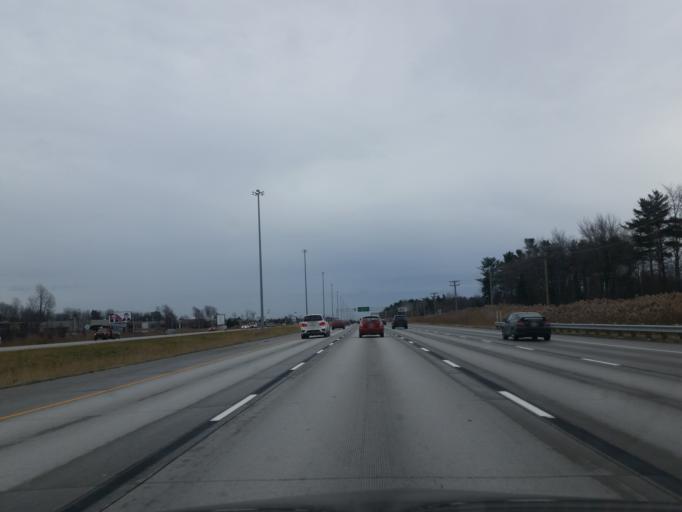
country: CA
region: Quebec
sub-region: Laurentides
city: Blainville
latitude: 45.6714
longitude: -73.9064
